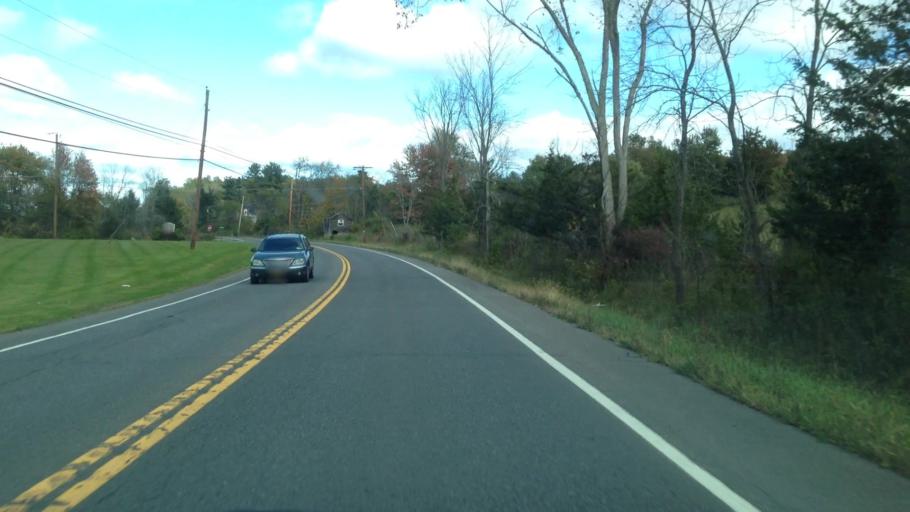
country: US
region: New York
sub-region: Ulster County
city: Tillson
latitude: 41.8044
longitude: -74.0624
